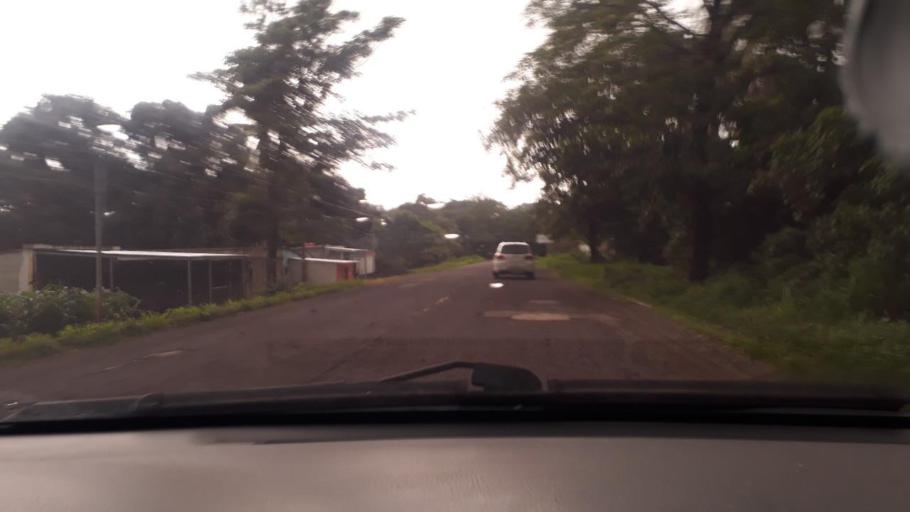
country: GT
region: Jutiapa
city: Jalpatagua
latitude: 14.1205
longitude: -89.9801
